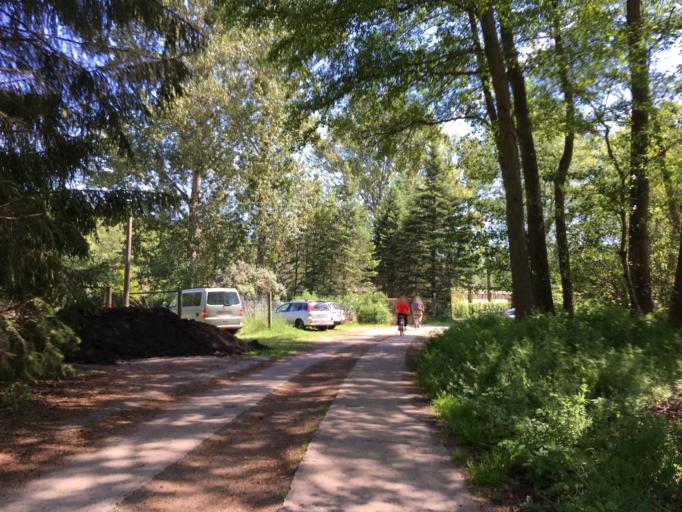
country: DE
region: Brandenburg
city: Eberswalde
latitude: 52.8502
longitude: 13.8562
